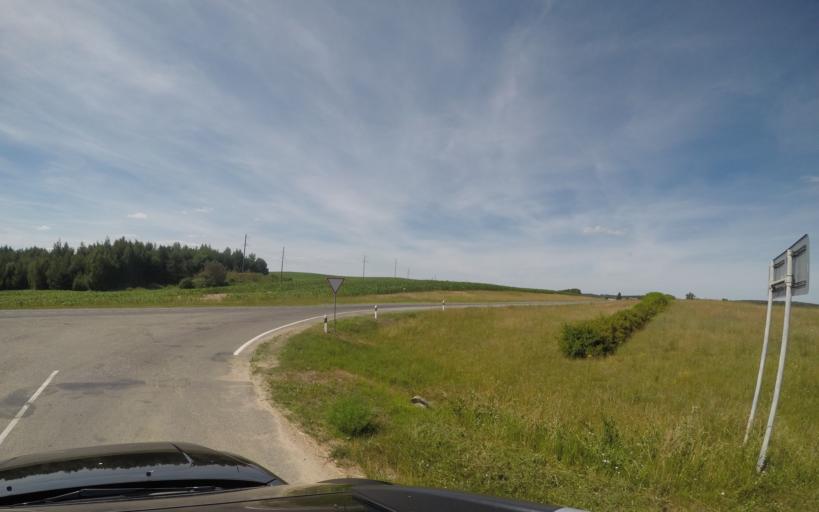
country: BY
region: Grodnenskaya
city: Hal'shany
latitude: 54.2696
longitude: 25.9910
